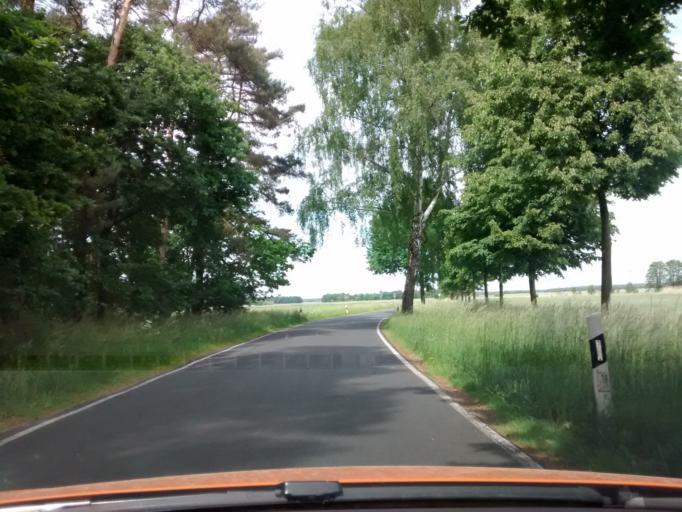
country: DE
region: Brandenburg
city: Ihlow
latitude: 51.8262
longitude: 13.2366
